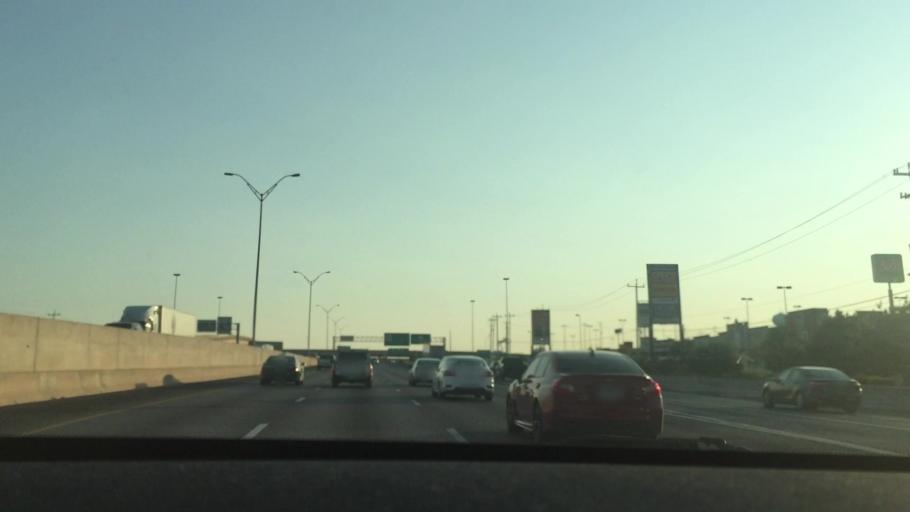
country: US
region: Texas
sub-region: Bexar County
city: Live Oak
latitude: 29.5719
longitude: -98.3289
